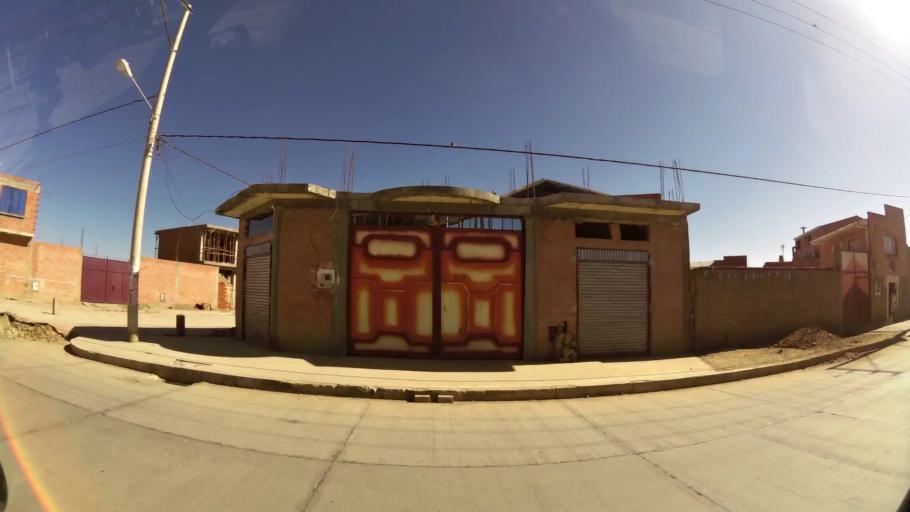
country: BO
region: La Paz
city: La Paz
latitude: -16.5291
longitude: -68.2311
